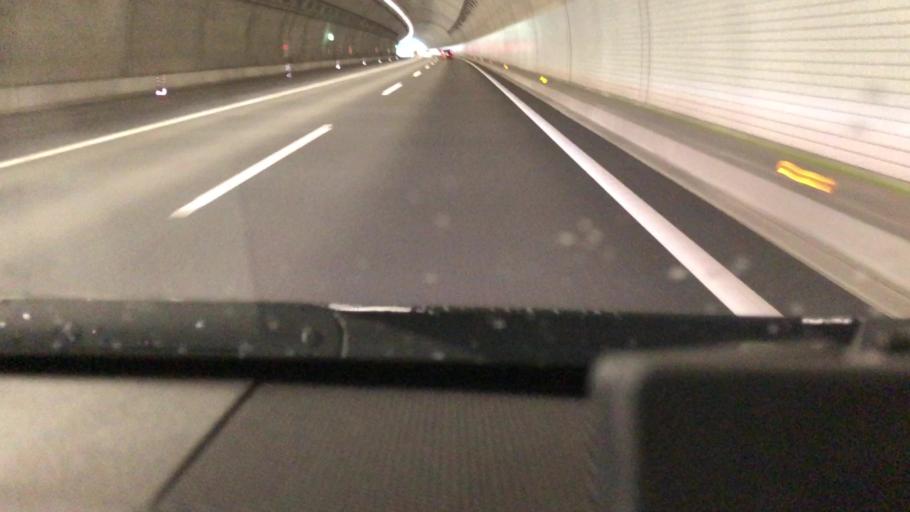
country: JP
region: Shizuoka
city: Kakegawa
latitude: 34.8419
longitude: 138.0225
